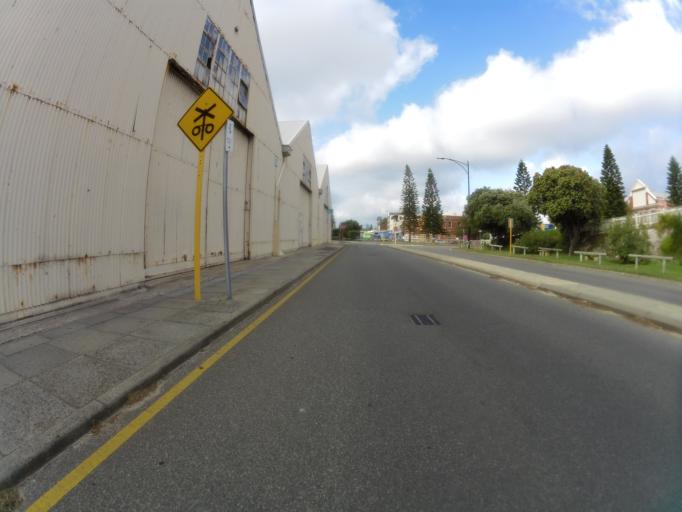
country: AU
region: Western Australia
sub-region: Fremantle
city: South Fremantle
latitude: -32.0551
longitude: 115.7409
